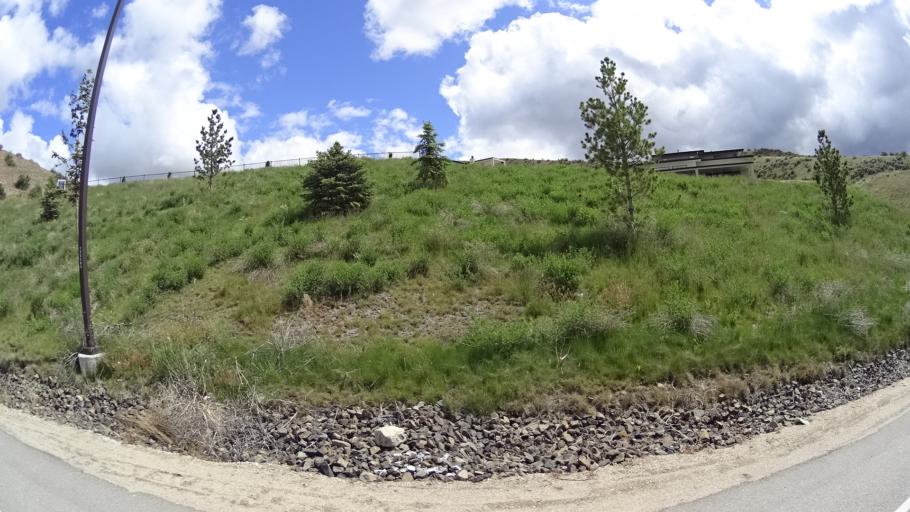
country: US
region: Idaho
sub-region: Ada County
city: Boise
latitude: 43.6617
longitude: -116.1899
